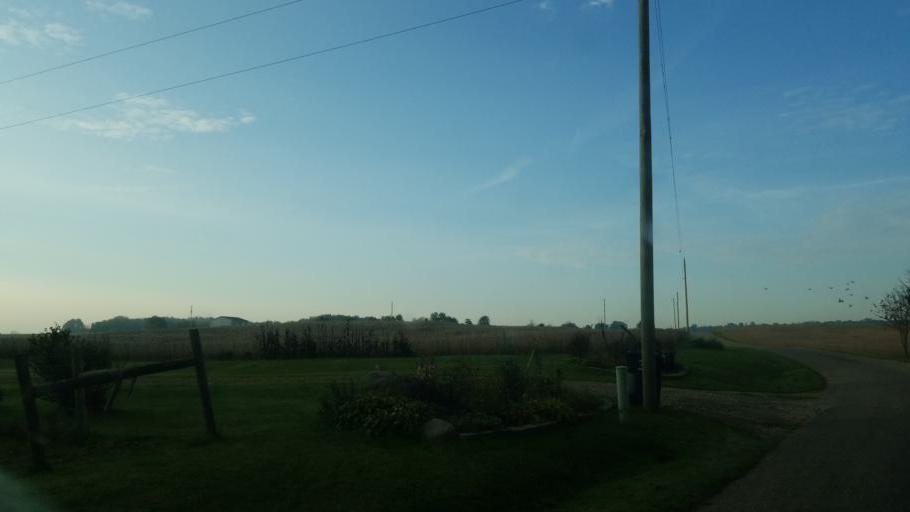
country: US
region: Ohio
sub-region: Knox County
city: Fredericktown
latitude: 40.4320
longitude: -82.6121
